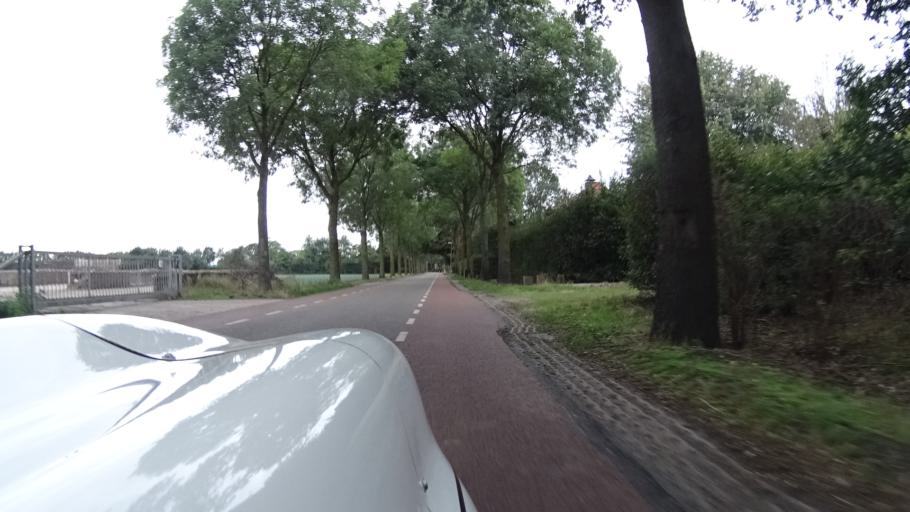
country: NL
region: North Brabant
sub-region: Gemeente Veghel
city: Mariaheide
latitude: 51.6329
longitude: 5.6037
